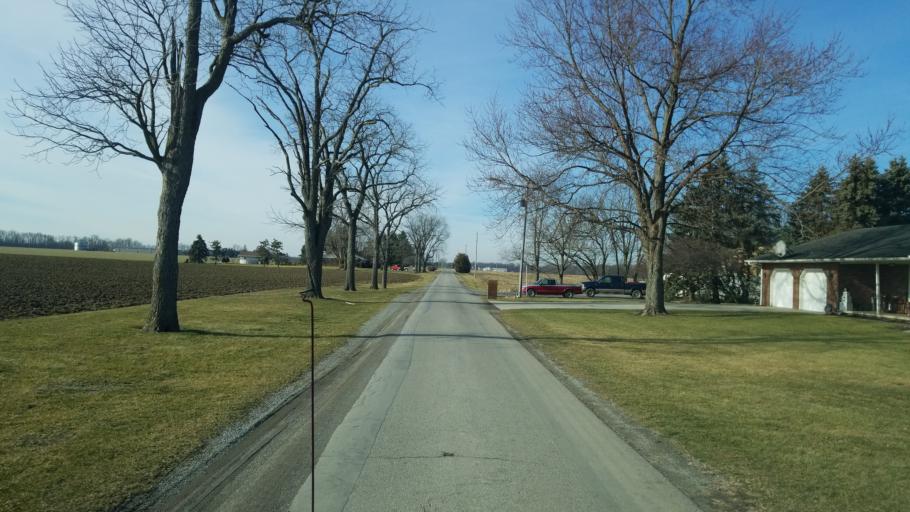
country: US
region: Ohio
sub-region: Putnam County
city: Pandora
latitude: 41.0074
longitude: -83.9466
